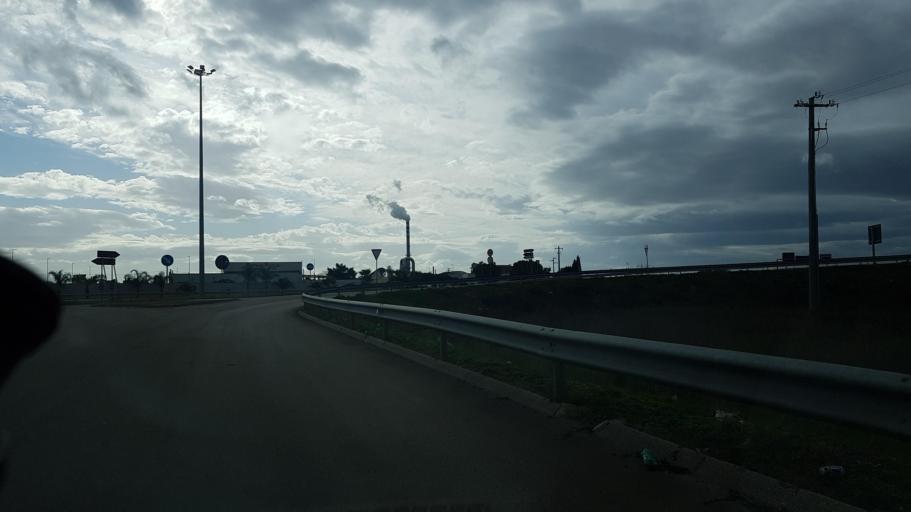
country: IT
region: Apulia
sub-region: Provincia di Brindisi
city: Francavilla Fontana
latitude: 40.5379
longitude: 17.5332
